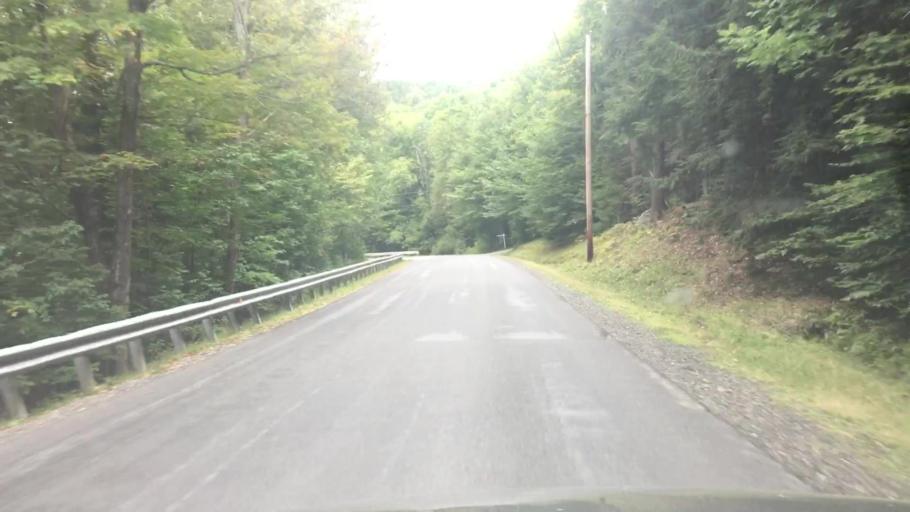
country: US
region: Vermont
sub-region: Windham County
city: Dover
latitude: 42.8444
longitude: -72.8302
